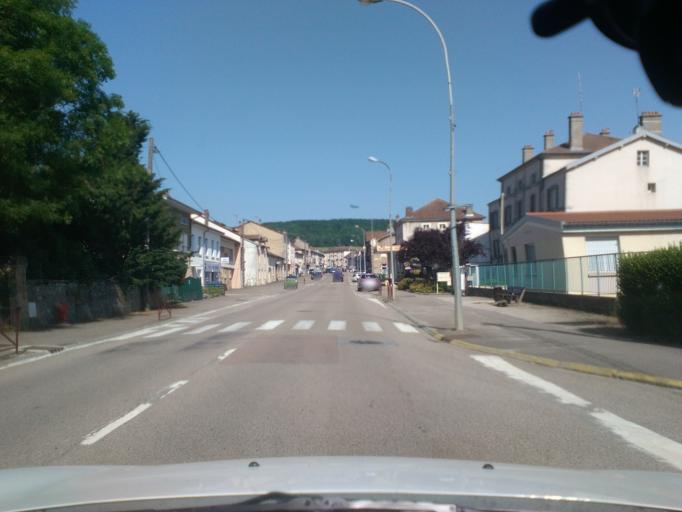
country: FR
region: Lorraine
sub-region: Departement des Vosges
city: Chatenois
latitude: 48.3011
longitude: 5.8379
